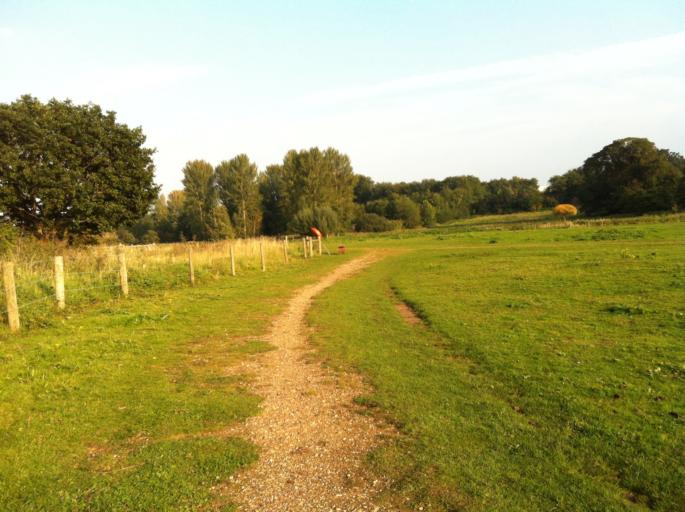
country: GB
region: England
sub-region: Norfolk
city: Bowthorpe
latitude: 52.6273
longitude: 1.2172
